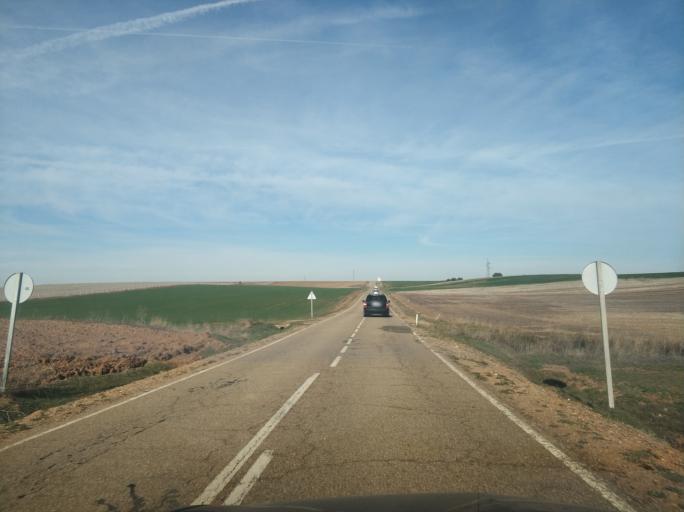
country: ES
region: Castille and Leon
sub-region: Provincia de Salamanca
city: Parada de Arriba
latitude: 40.9908
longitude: -5.8028
